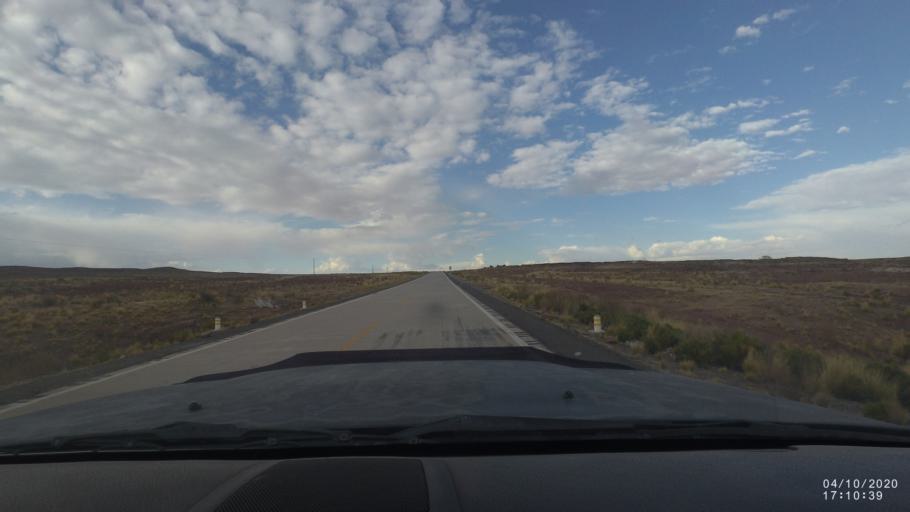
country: BO
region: Oruro
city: Oruro
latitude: -18.3287
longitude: -67.5823
